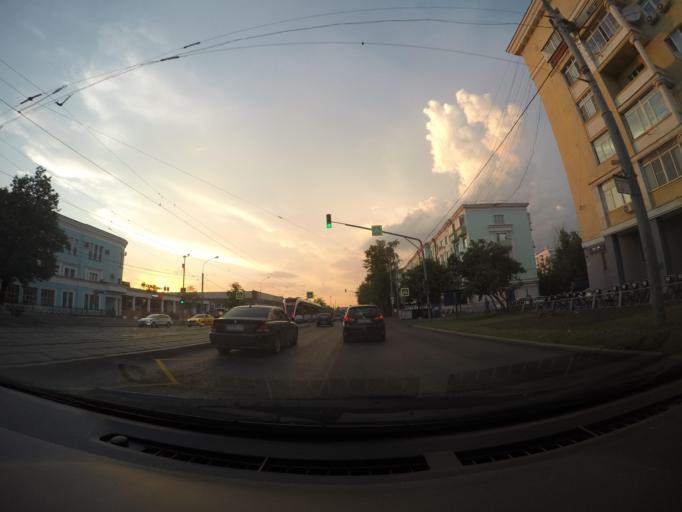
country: RU
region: Moscow
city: Lefortovo
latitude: 55.7734
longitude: 37.7254
